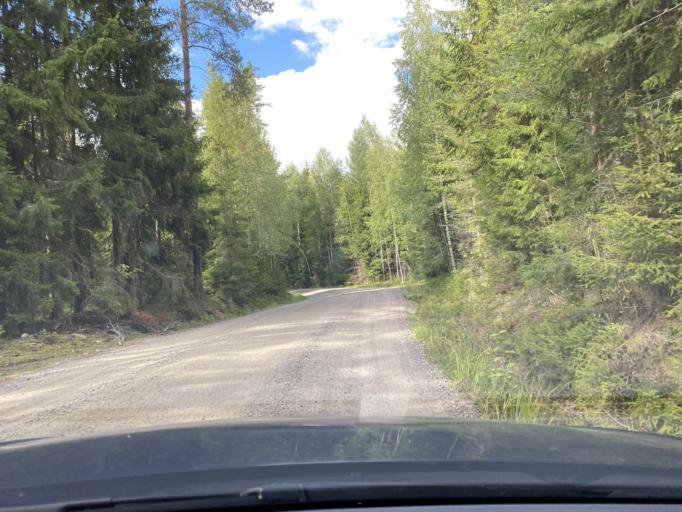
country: FI
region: Haeme
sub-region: Forssa
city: Humppila
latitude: 61.0606
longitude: 23.2588
